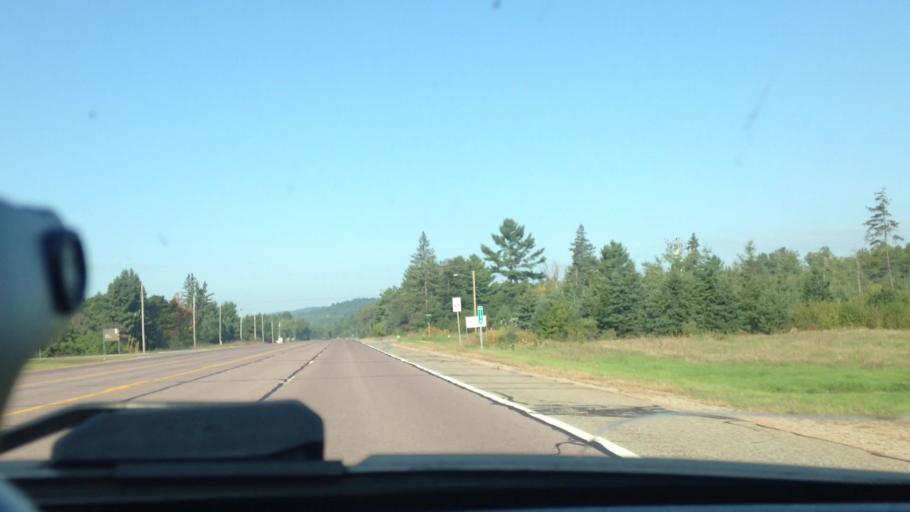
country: US
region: Michigan
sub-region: Dickinson County
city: Quinnesec
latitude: 45.8019
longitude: -87.9575
